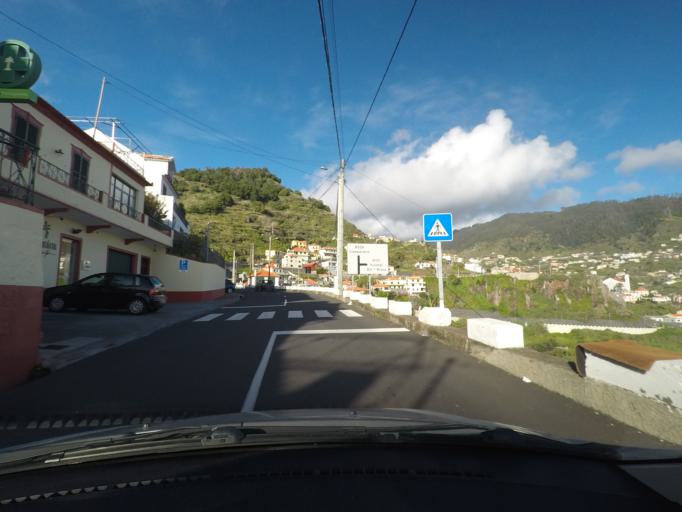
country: PT
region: Madeira
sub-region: Ribeira Brava
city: Campanario
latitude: 32.6670
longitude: -17.0366
